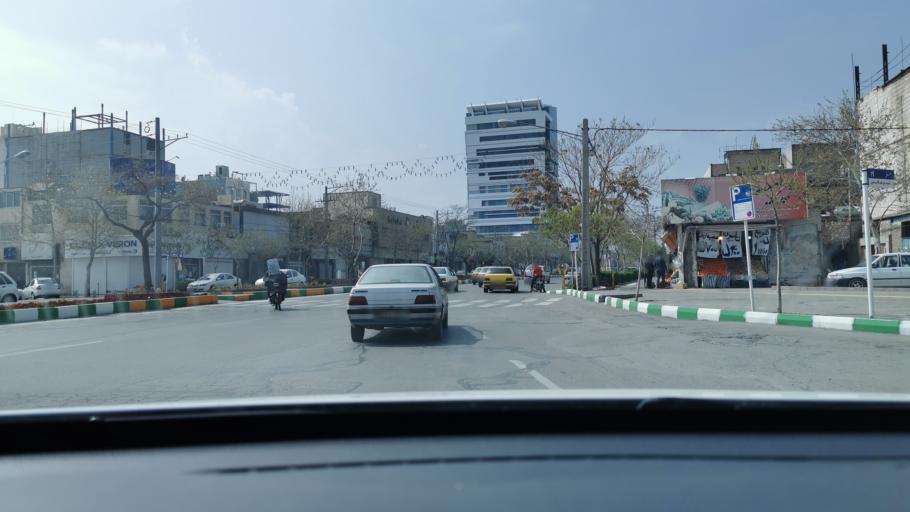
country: IR
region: Razavi Khorasan
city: Mashhad
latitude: 36.3294
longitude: 59.5256
